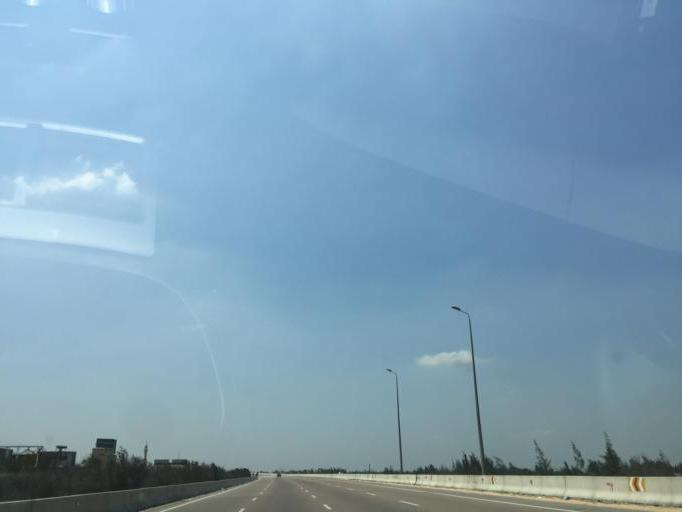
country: EG
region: Al Buhayrah
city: Beheira
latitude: 30.5316
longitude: 30.2253
